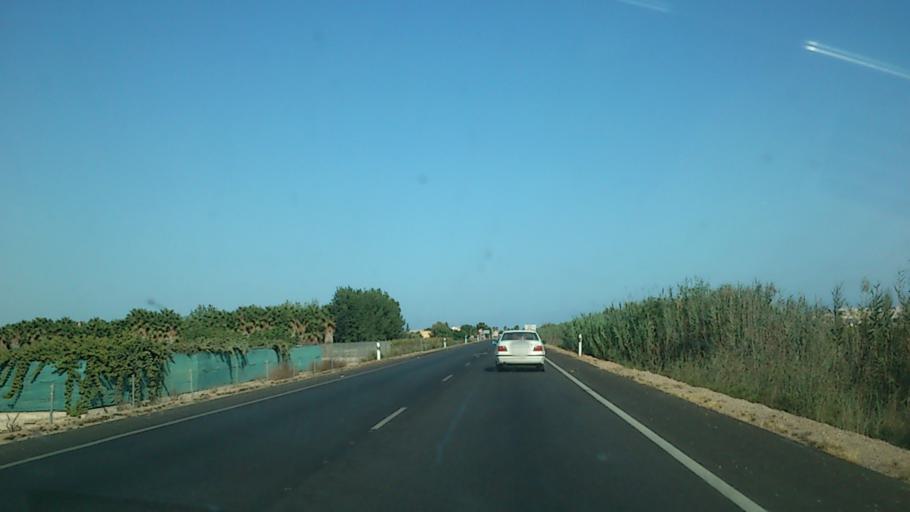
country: ES
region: Valencia
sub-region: Provincia de Alicante
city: Daya Vieja
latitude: 38.0975
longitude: -0.7384
